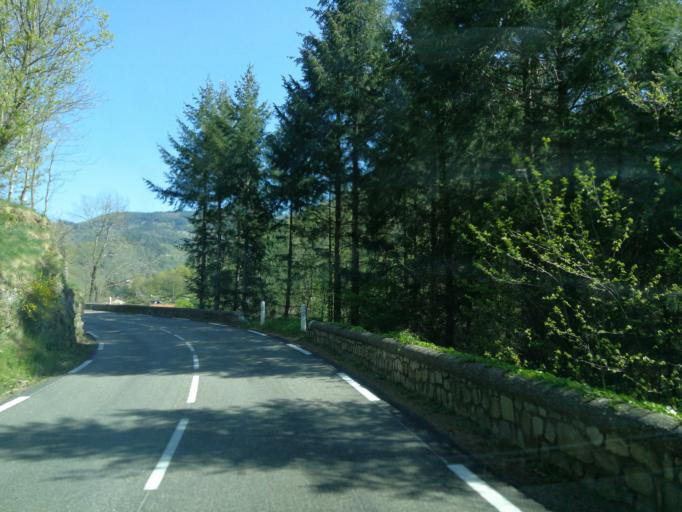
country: FR
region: Rhone-Alpes
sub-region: Departement de l'Ardeche
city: Le Cheylard
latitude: 44.8974
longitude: 4.4853
